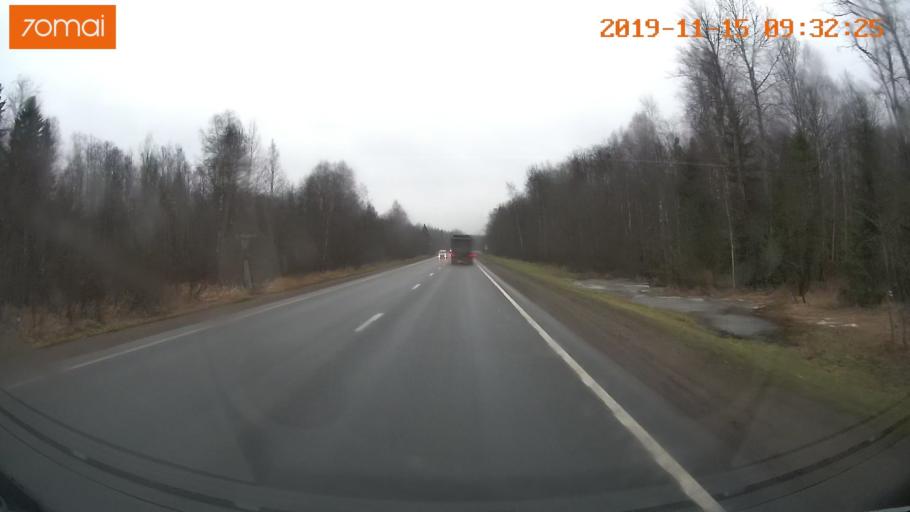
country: RU
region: Vologda
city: Sheksna
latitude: 59.2719
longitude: 38.3333
